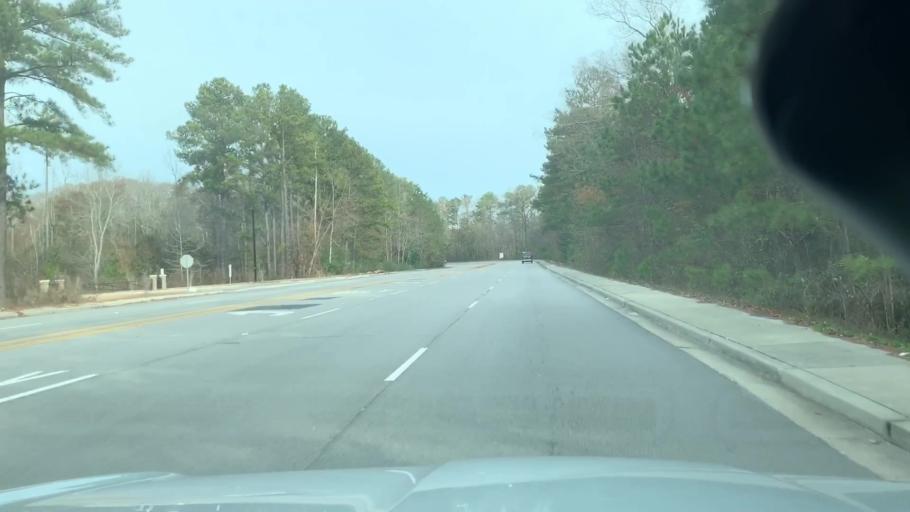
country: US
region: South Carolina
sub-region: Richland County
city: Dentsville
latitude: 34.0647
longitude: -80.9475
